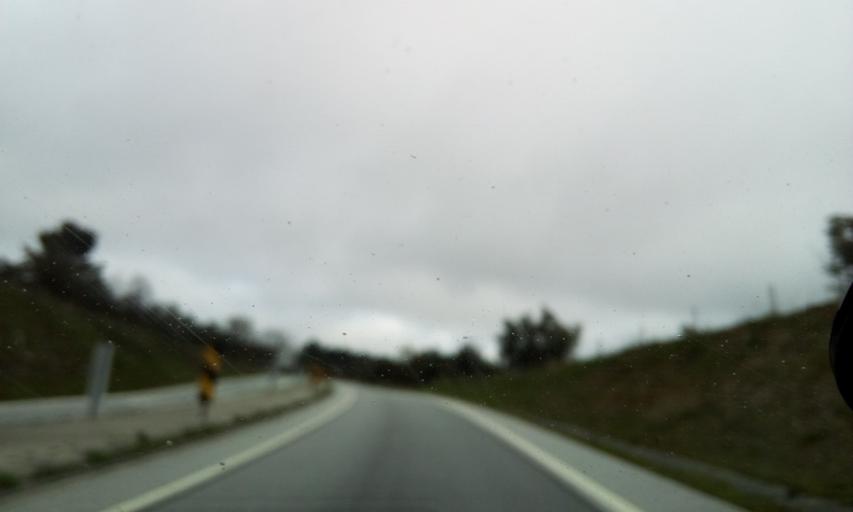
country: PT
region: Guarda
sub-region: Fornos de Algodres
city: Fornos de Algodres
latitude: 40.6276
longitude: -7.5040
